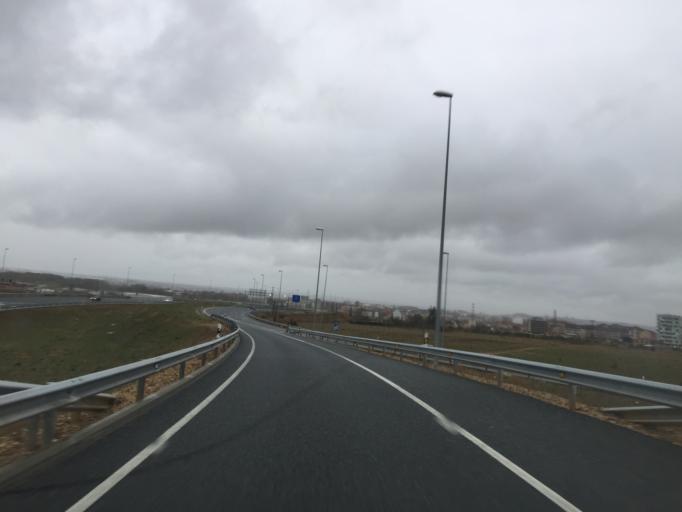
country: ES
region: Castille and Leon
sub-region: Provincia de Leon
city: Leon
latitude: 42.5712
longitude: -5.5459
